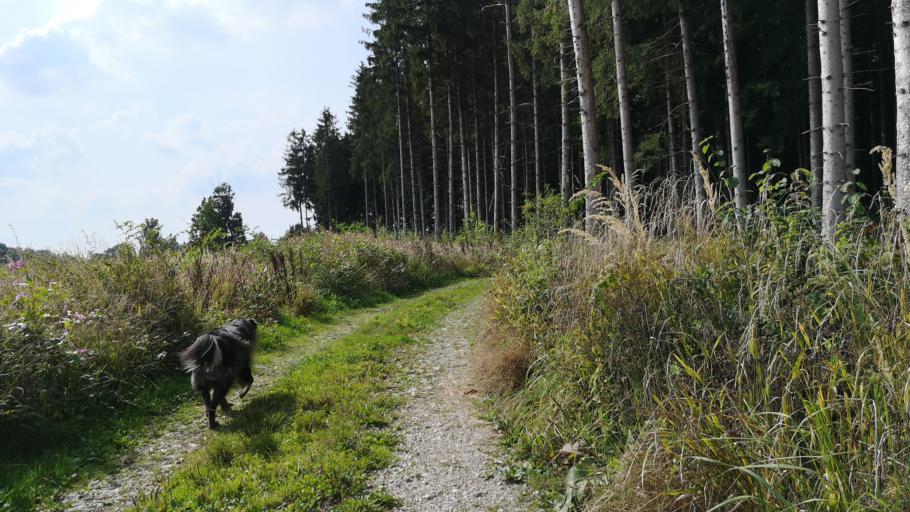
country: DE
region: Bavaria
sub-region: Upper Bavaria
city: Poing
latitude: 48.1784
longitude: 11.8294
